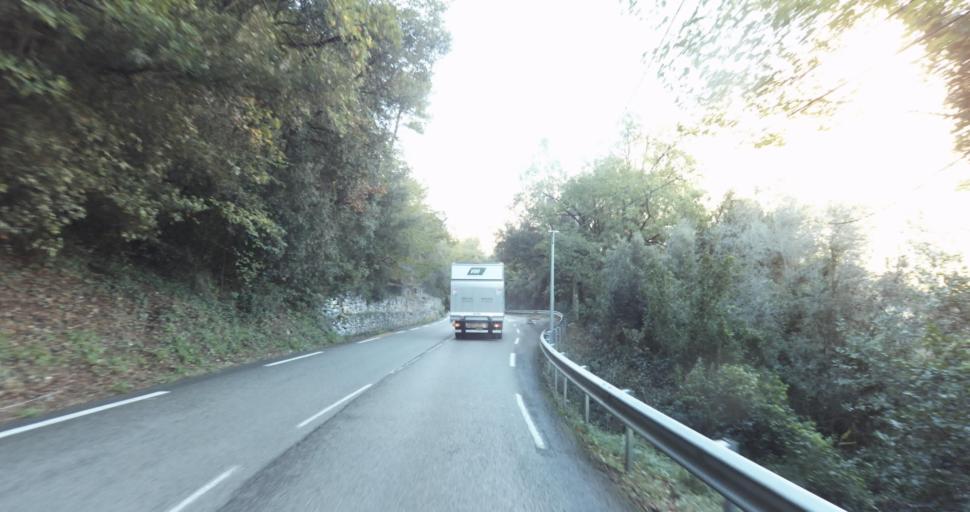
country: FR
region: Provence-Alpes-Cote d'Azur
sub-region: Departement des Alpes-Maritimes
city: Saint-Jeannet
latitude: 43.7446
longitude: 7.1309
